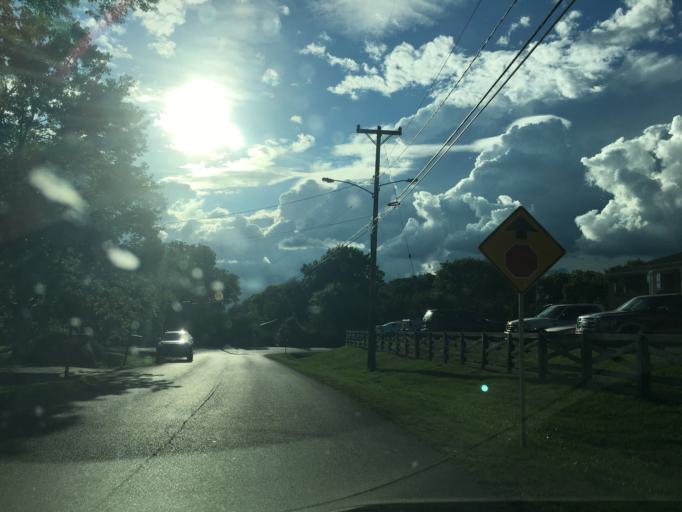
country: US
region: Tennessee
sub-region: Davidson County
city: Oak Hill
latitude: 36.0678
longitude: -86.7294
